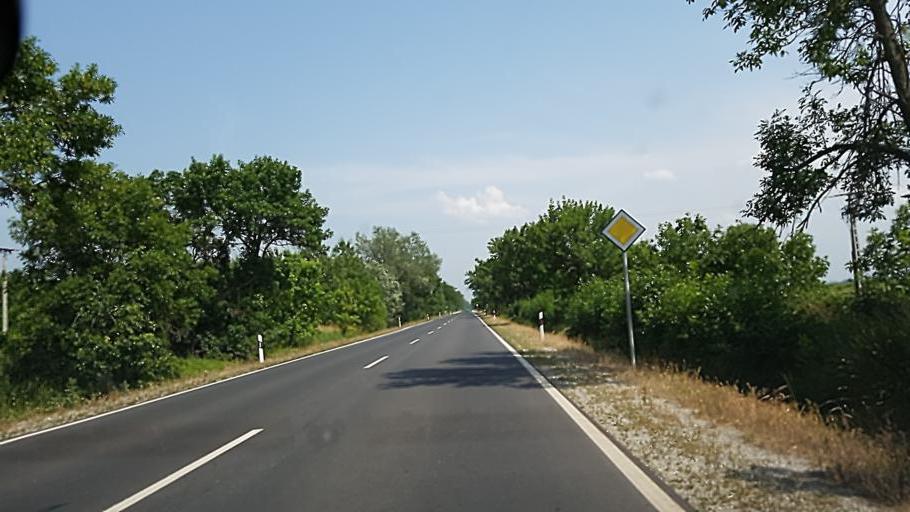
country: HU
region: Heves
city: Poroszlo
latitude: 47.6530
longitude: 20.6108
